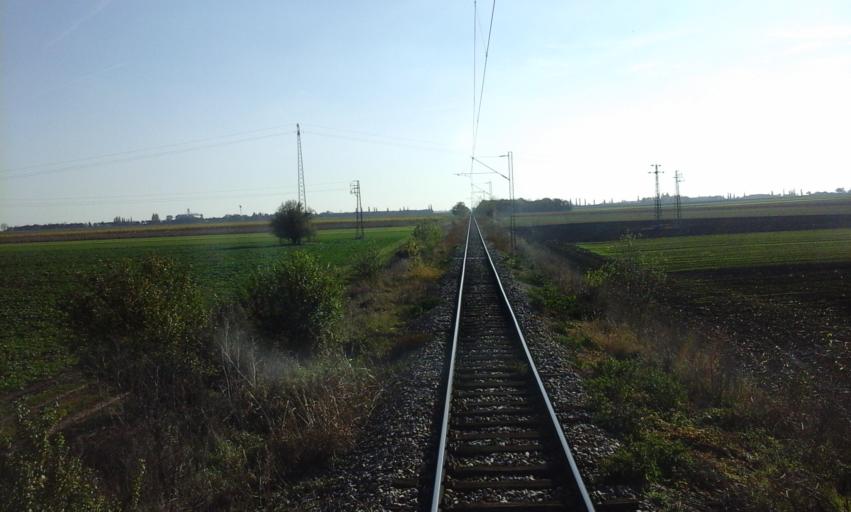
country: RS
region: Autonomna Pokrajina Vojvodina
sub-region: Severnobacki Okrug
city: Backa Topola
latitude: 45.7924
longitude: 19.6474
